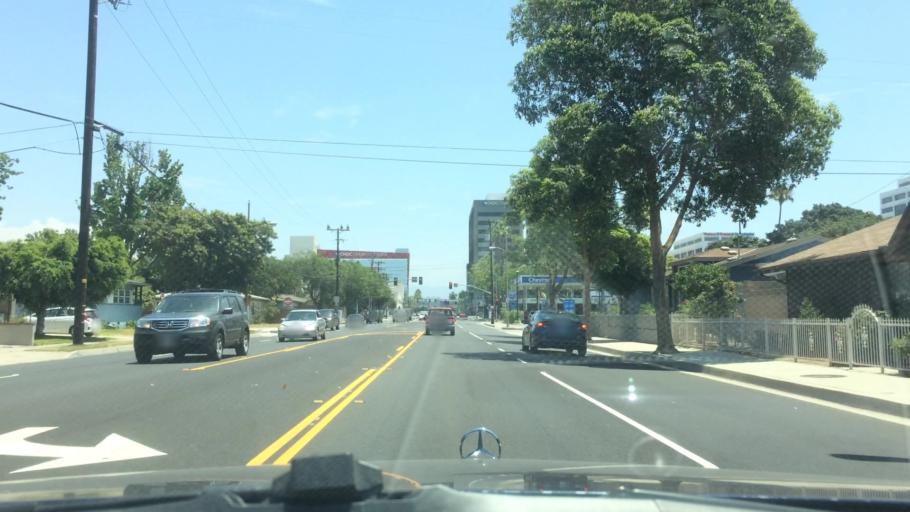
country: US
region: California
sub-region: Orange County
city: Orange
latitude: 33.7803
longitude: -117.8711
